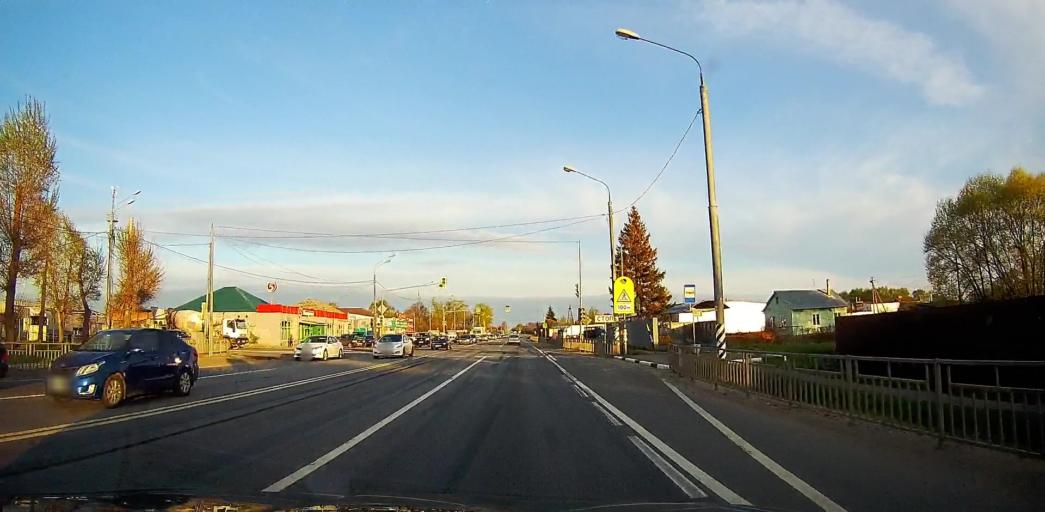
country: RU
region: Moskovskaya
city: Troitskoye
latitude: 55.2490
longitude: 38.5265
